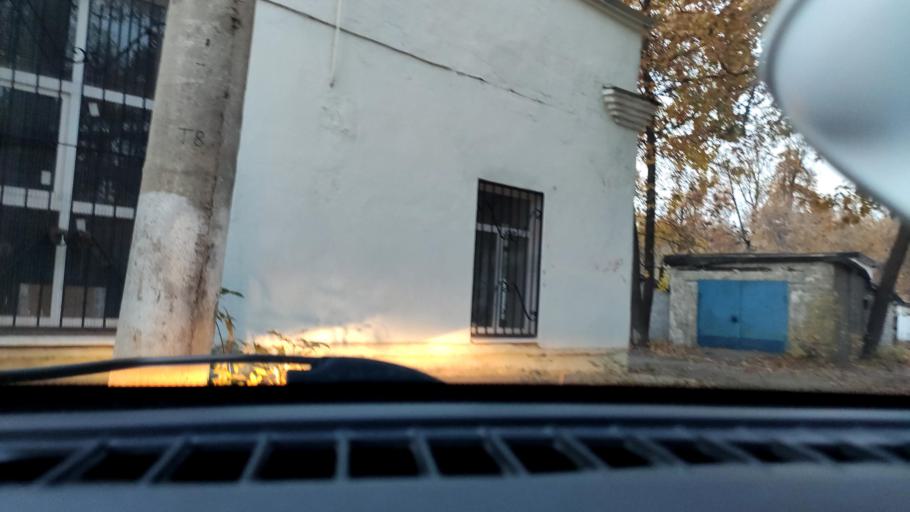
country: RU
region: Samara
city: Samara
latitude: 53.2675
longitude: 50.2415
